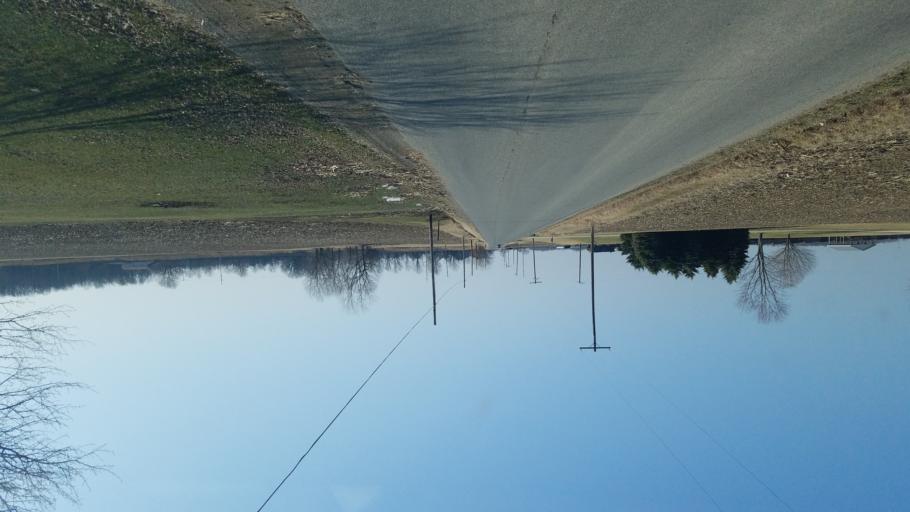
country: US
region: Ohio
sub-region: Crawford County
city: Crestline
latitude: 40.7989
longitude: -82.7309
